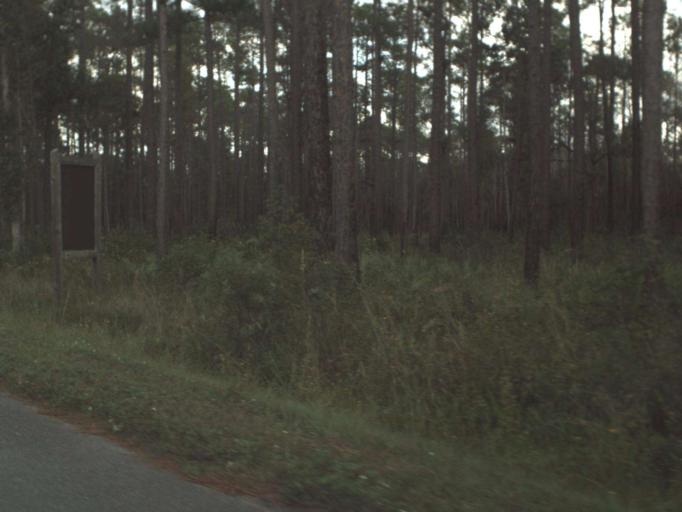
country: US
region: Florida
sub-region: Wakulla County
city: Crawfordville
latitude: 30.0483
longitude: -84.4939
